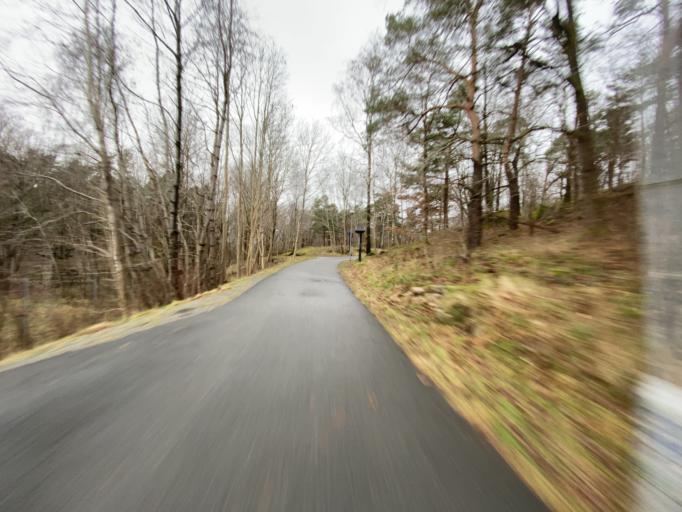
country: SE
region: Vaestra Goetaland
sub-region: Molndal
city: Moelndal
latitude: 57.7100
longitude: 12.0395
